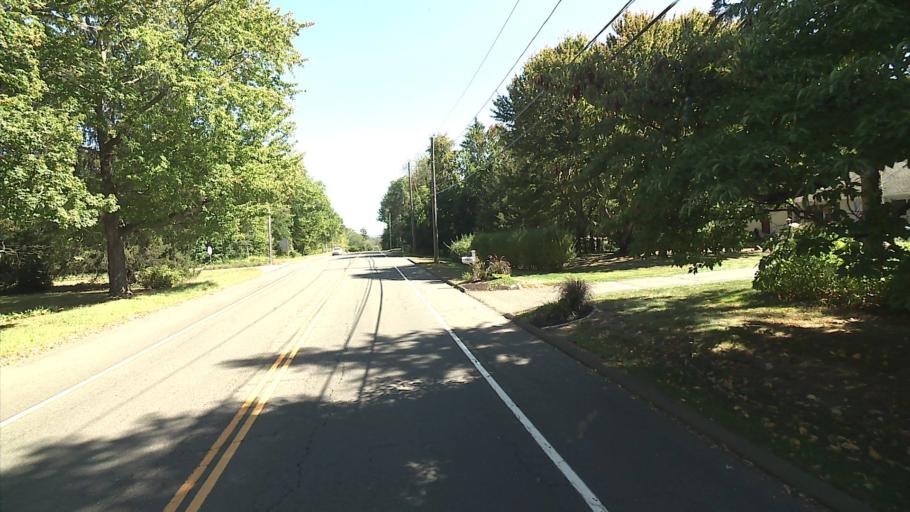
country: US
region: Connecticut
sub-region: New Haven County
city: Cheshire Village
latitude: 41.5005
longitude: -72.8748
